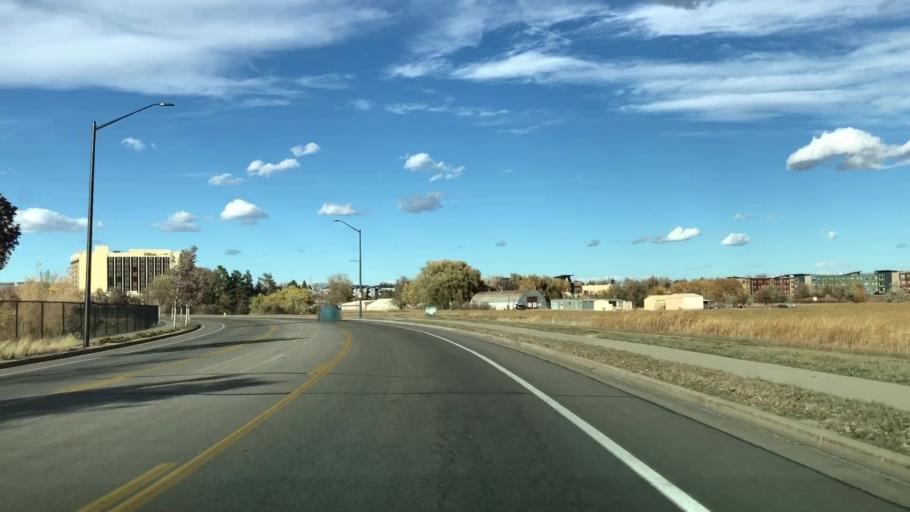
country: US
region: Colorado
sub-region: Larimer County
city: Fort Collins
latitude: 40.5619
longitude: -105.0835
